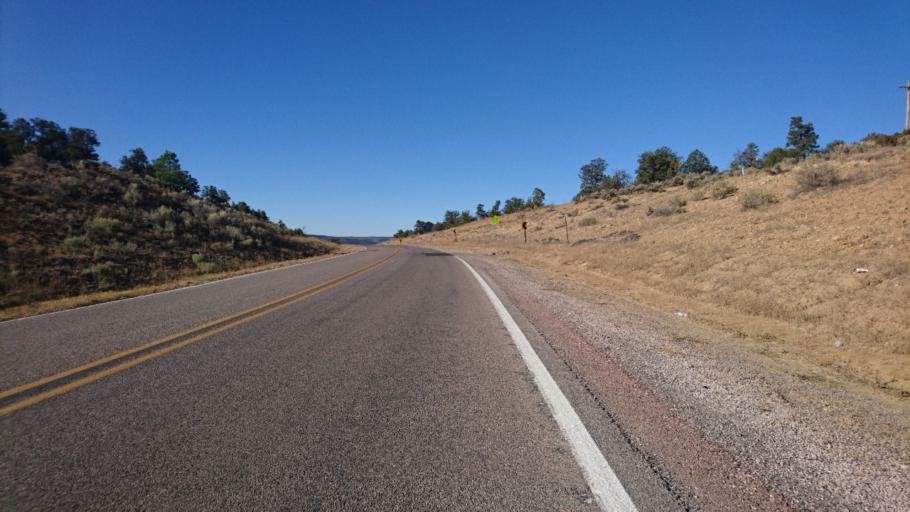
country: US
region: New Mexico
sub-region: McKinley County
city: Black Rock
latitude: 35.1310
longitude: -108.5245
